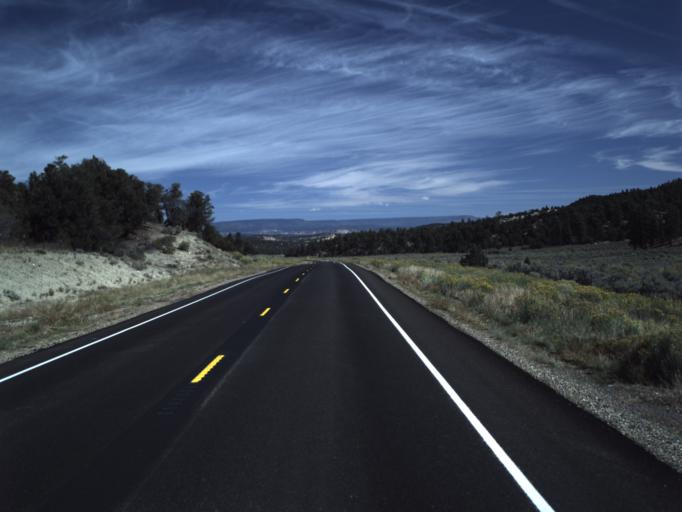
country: US
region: Utah
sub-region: Garfield County
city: Panguitch
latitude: 37.6555
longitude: -111.8381
